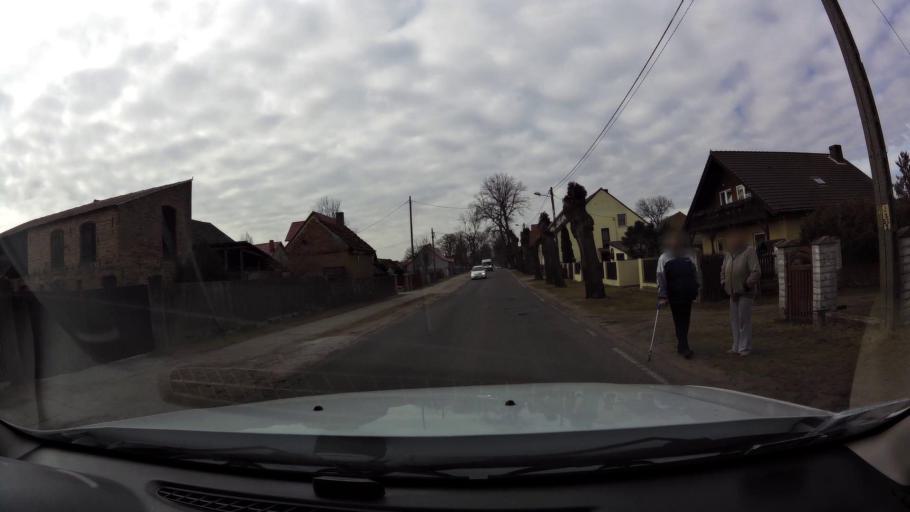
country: PL
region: West Pomeranian Voivodeship
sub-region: Powiat mysliborski
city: Debno
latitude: 52.7102
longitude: 14.6521
